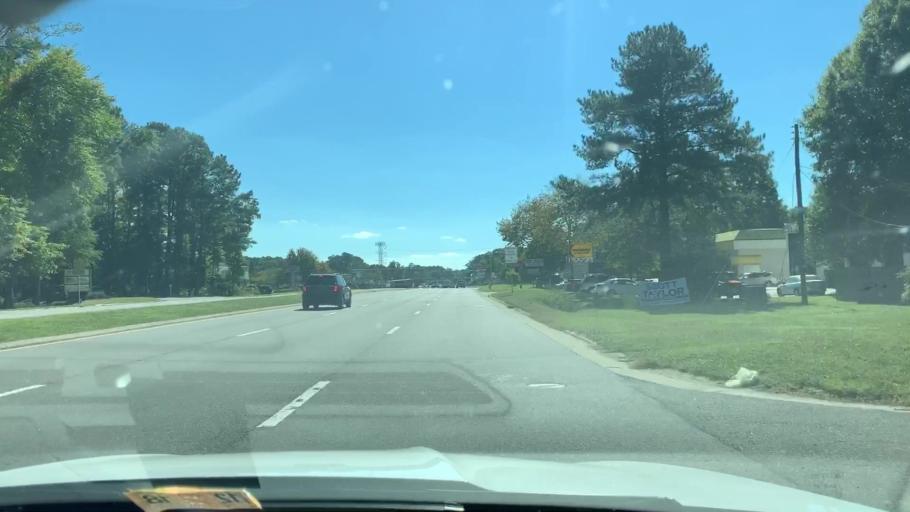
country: US
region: Virginia
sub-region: York County
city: Yorktown
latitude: 37.1499
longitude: -76.4600
